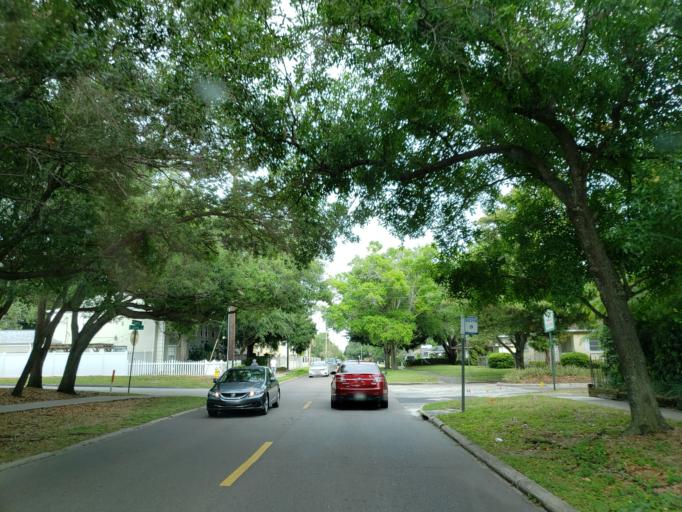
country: US
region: Florida
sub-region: Hillsborough County
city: Tampa
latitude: 27.9375
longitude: -82.4998
